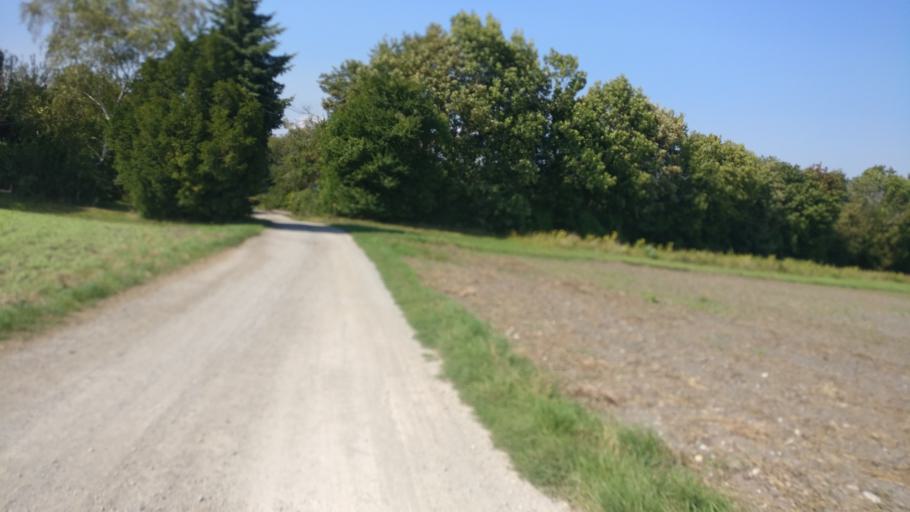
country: AT
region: Lower Austria
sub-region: Politischer Bezirk Wien-Umgebung
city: Moosbrunn
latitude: 47.9924
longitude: 16.4162
